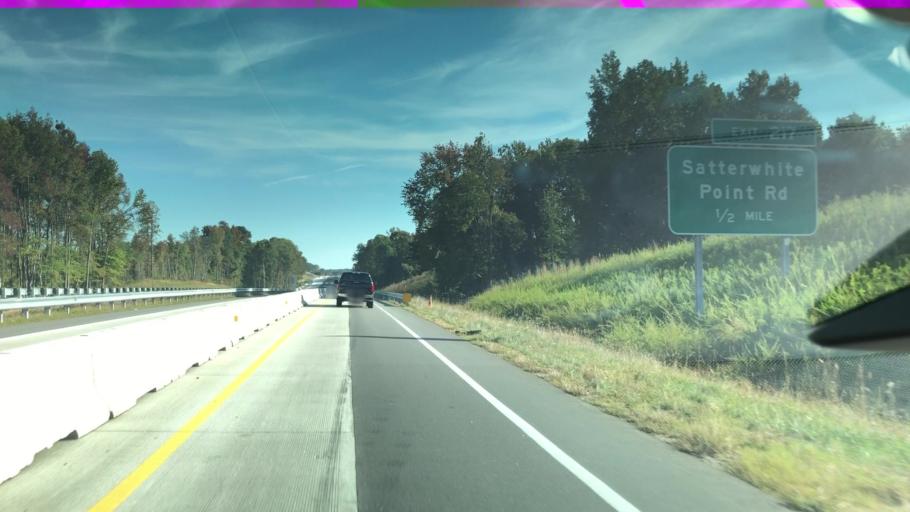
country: US
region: North Carolina
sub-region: Vance County
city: Henderson
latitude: 36.3551
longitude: -78.3845
